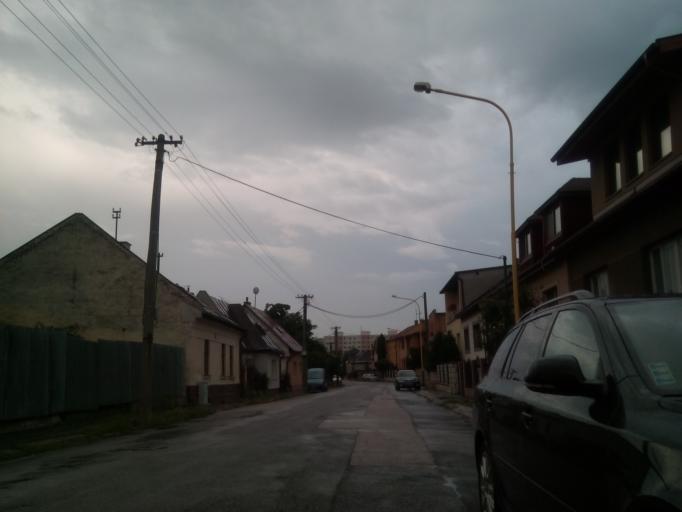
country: SK
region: Kosicky
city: Kosice
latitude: 48.7358
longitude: 21.2586
